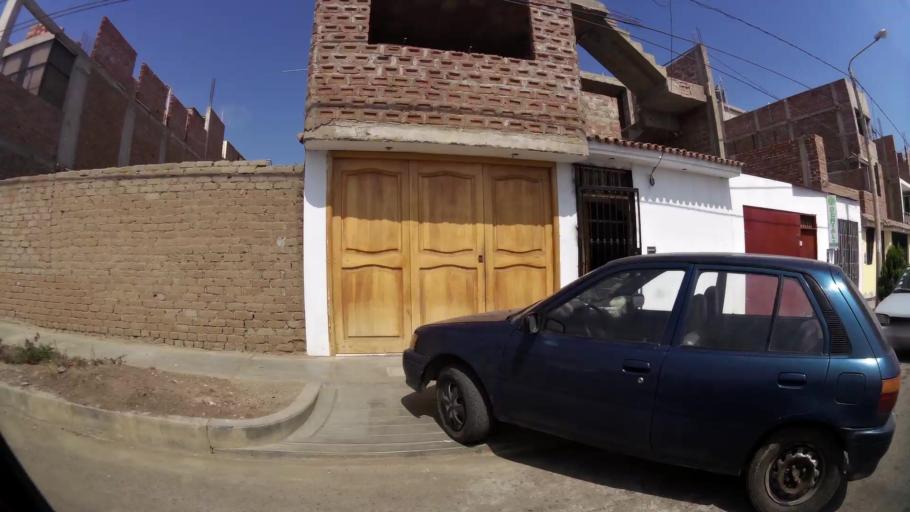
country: PE
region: La Libertad
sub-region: Provincia de Trujillo
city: Buenos Aires
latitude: -8.1251
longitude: -79.0437
